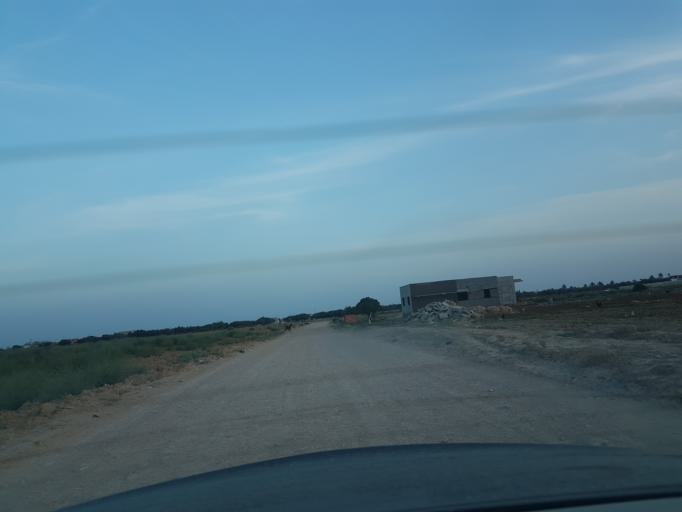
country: TN
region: Safaqis
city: Sfax
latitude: 34.7073
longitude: 10.6901
